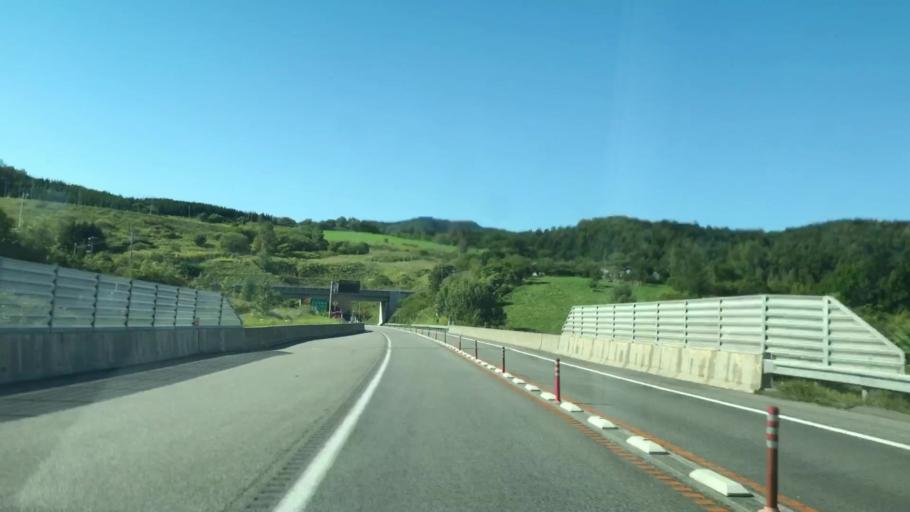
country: JP
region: Hokkaido
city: Date
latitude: 42.5503
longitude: 140.7902
